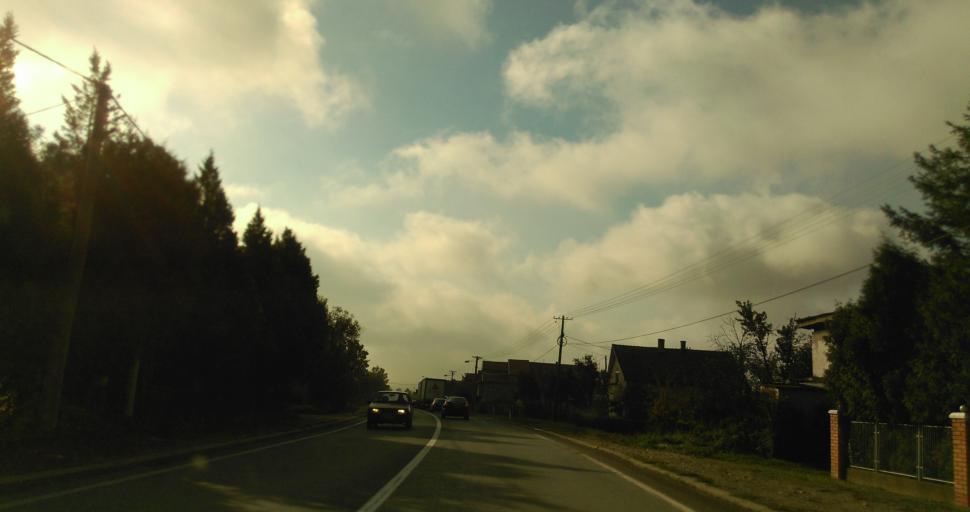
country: RS
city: Stepojevac
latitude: 44.5194
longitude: 20.2926
